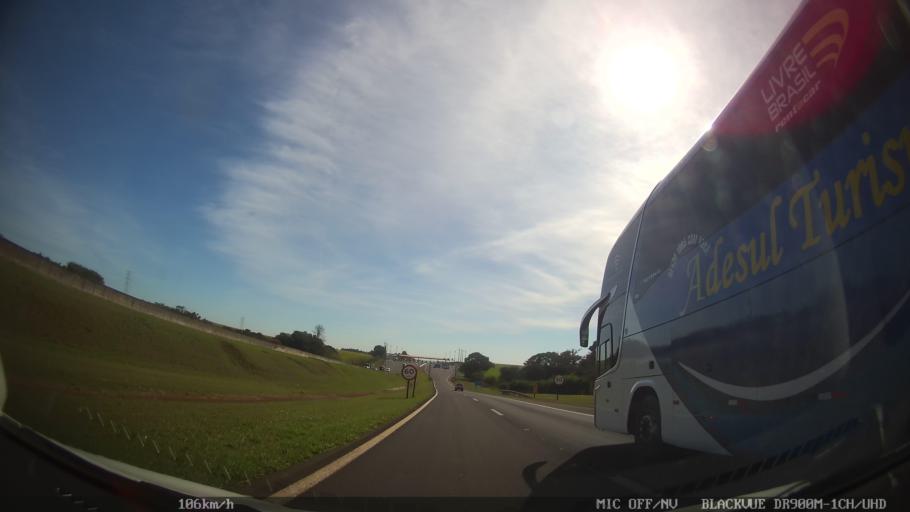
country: BR
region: Sao Paulo
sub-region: Leme
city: Leme
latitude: -22.2549
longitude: -47.3897
